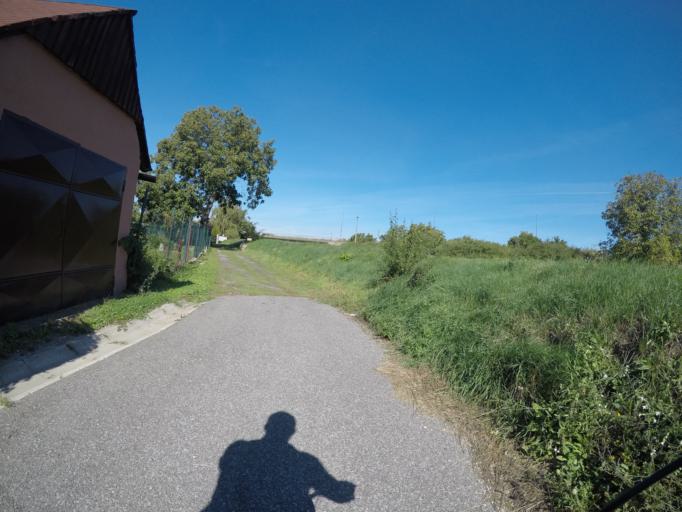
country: SK
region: Trenciansky
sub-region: Okres Nove Mesto nad Vahom
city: Nove Mesto nad Vahom
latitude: 48.7638
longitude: 17.8406
